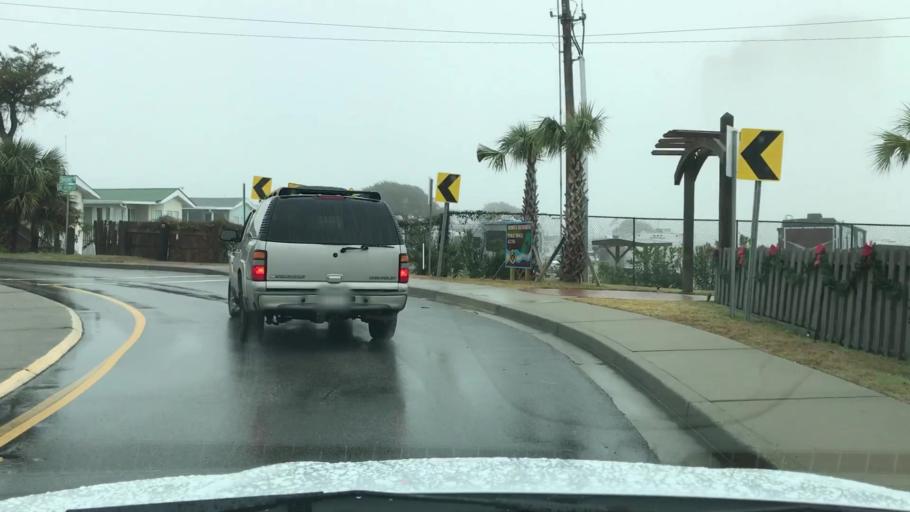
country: US
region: South Carolina
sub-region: Horry County
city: North Myrtle Beach
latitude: 33.7634
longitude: -78.7851
